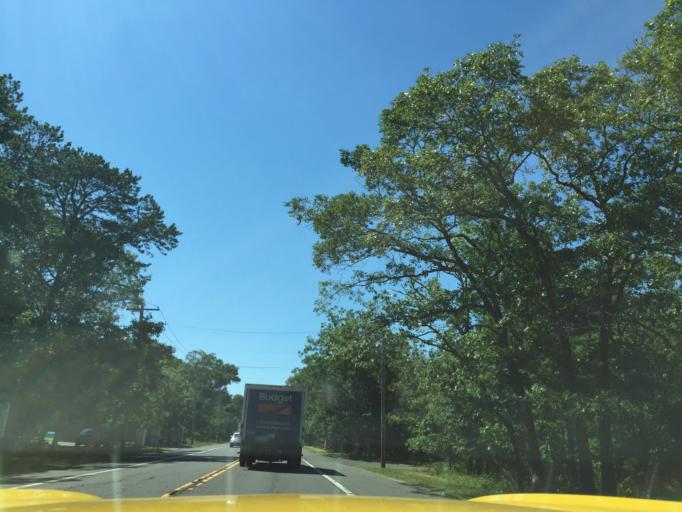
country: US
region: New York
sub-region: Suffolk County
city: Sag Harbor
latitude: 40.9917
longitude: -72.2677
